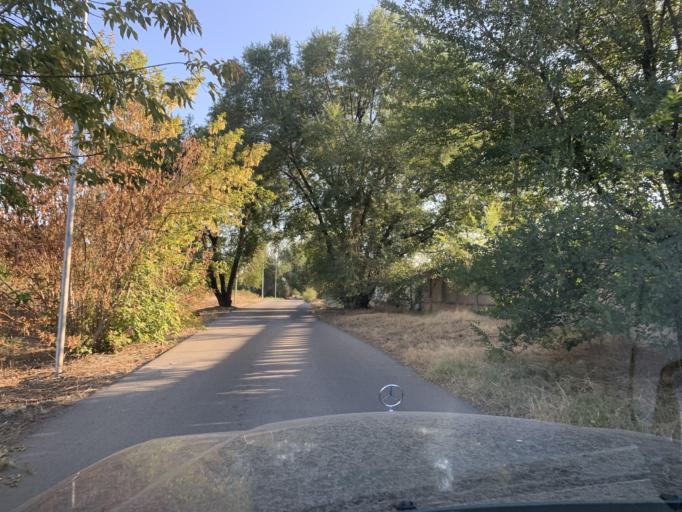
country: KZ
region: Almaty Oblysy
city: Energeticheskiy
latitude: 43.3926
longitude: 77.0003
